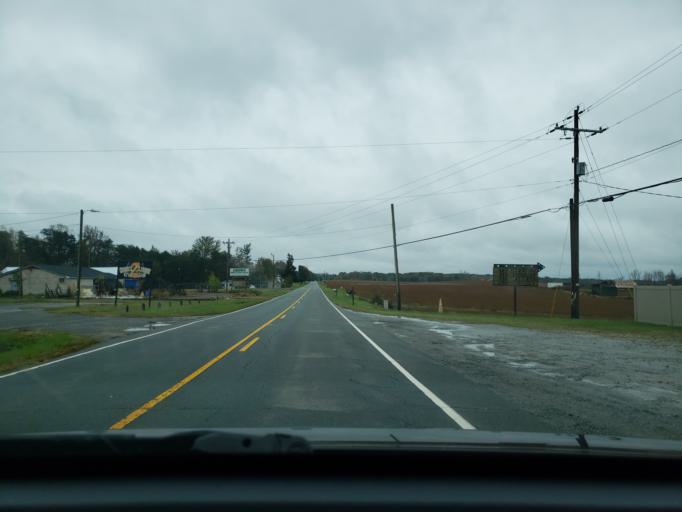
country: US
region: North Carolina
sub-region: Stokes County
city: Walnut Cove
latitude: 36.3342
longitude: -80.1494
